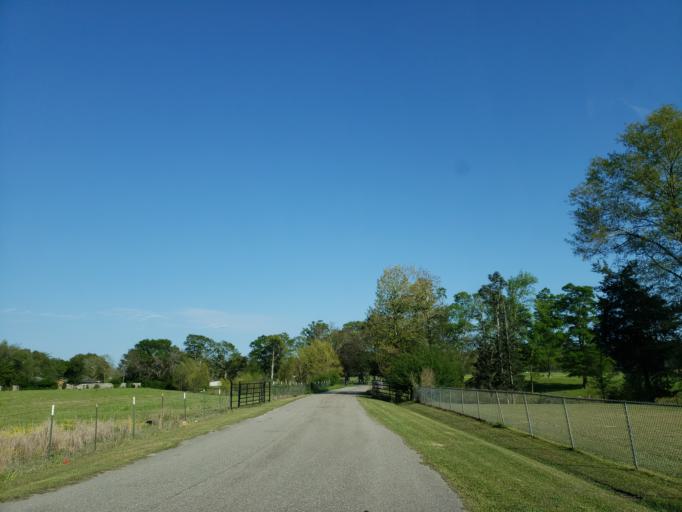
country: US
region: Mississippi
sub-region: Jones County
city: Ellisville
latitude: 31.6777
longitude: -89.3077
